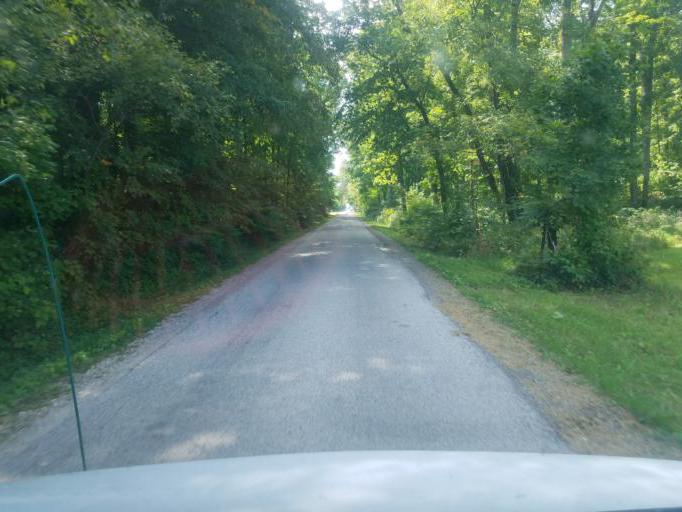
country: US
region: Ohio
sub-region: Marion County
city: Marion
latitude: 40.5073
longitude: -83.1175
